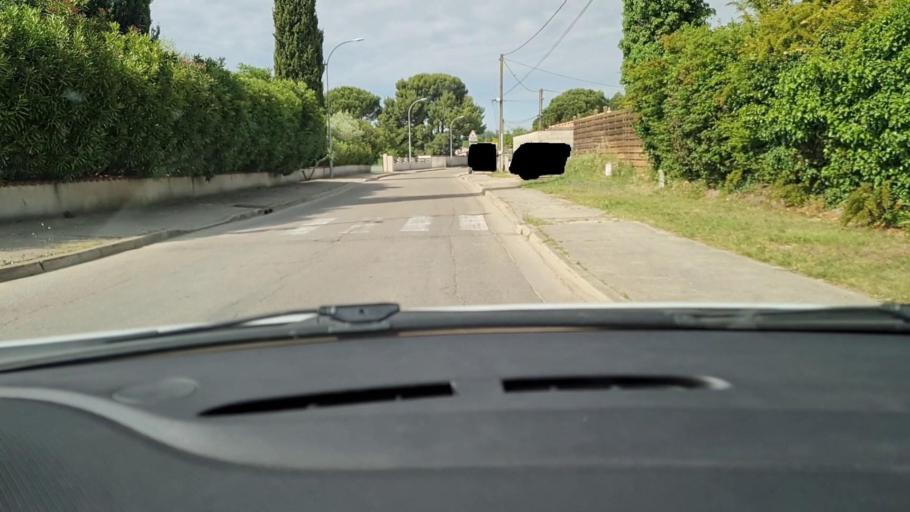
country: FR
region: Languedoc-Roussillon
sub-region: Departement du Gard
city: Jonquieres-Saint-Vincent
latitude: 43.8242
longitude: 4.5613
